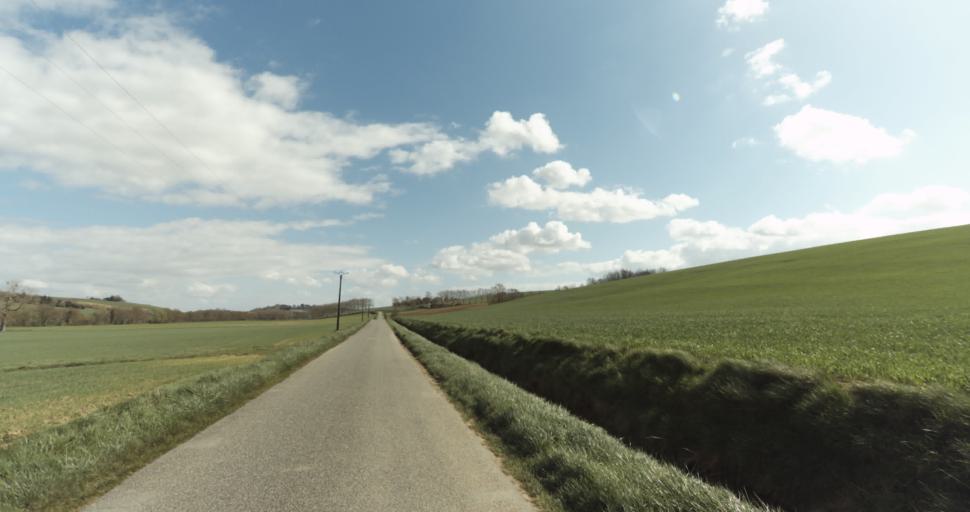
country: FR
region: Midi-Pyrenees
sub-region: Departement de la Haute-Garonne
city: Auterive
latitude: 43.3672
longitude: 1.5217
